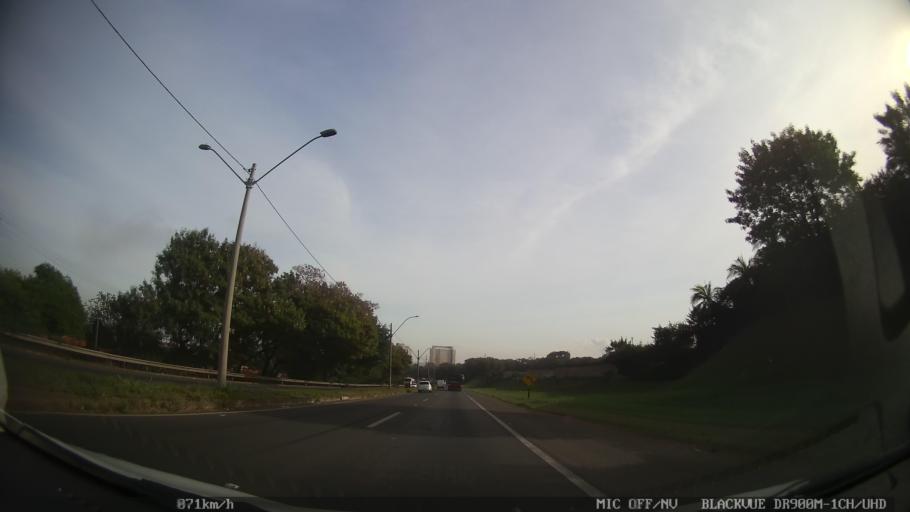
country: BR
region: Sao Paulo
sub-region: Piracicaba
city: Piracicaba
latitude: -22.6903
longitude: -47.6665
